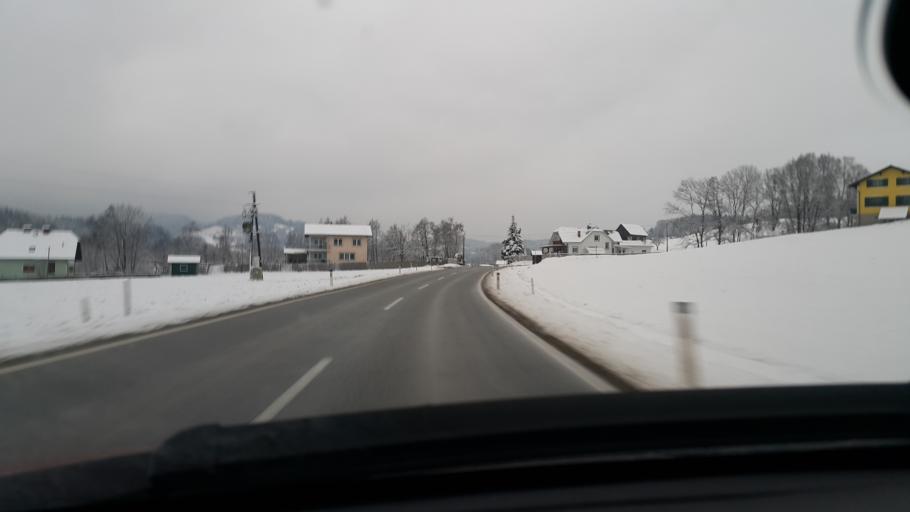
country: AT
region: Styria
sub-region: Politischer Bezirk Graz-Umgebung
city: Sankt Oswald bei Plankenwarth
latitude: 47.0676
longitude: 15.2718
